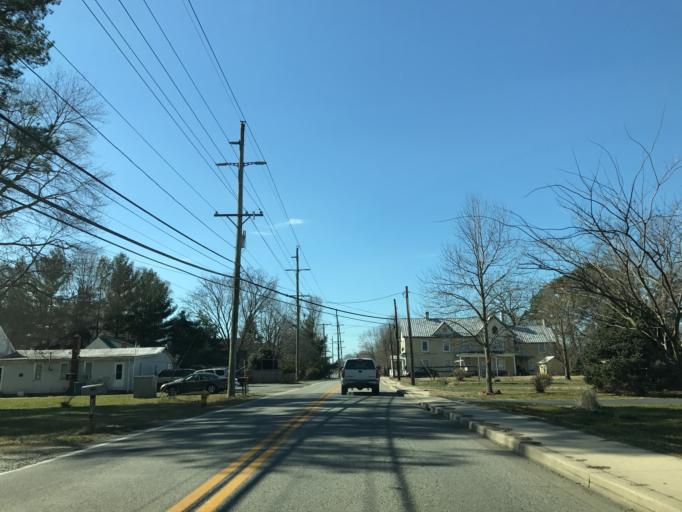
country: US
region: Maryland
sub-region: Queen Anne's County
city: Grasonville
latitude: 38.9597
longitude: -76.1954
